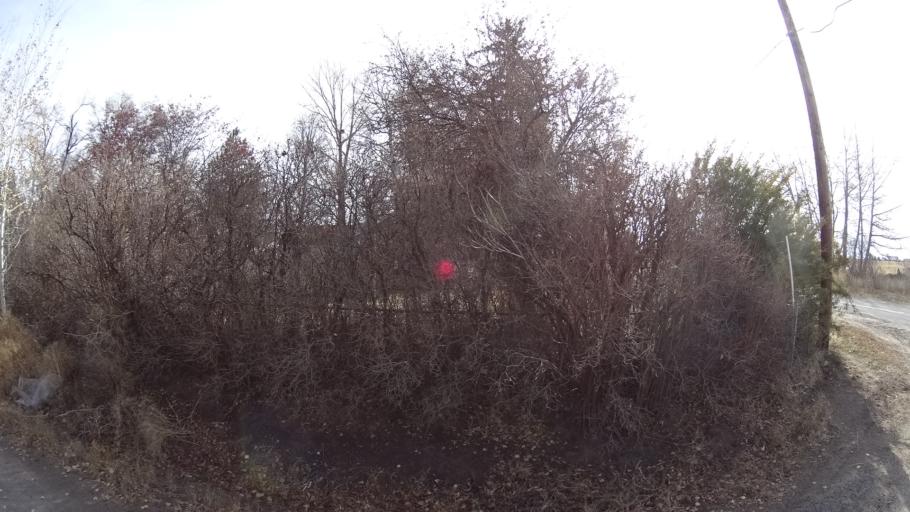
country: US
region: Oregon
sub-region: Klamath County
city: Klamath Falls
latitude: 41.9716
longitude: -121.9213
